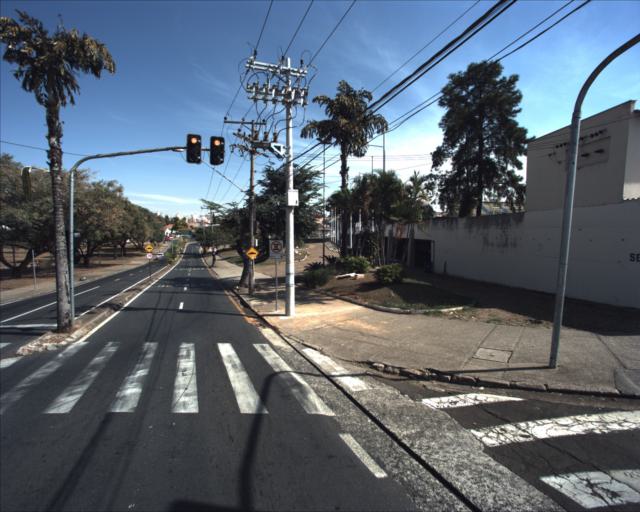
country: BR
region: Sao Paulo
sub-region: Sorocaba
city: Sorocaba
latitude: -23.4902
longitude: -47.4478
